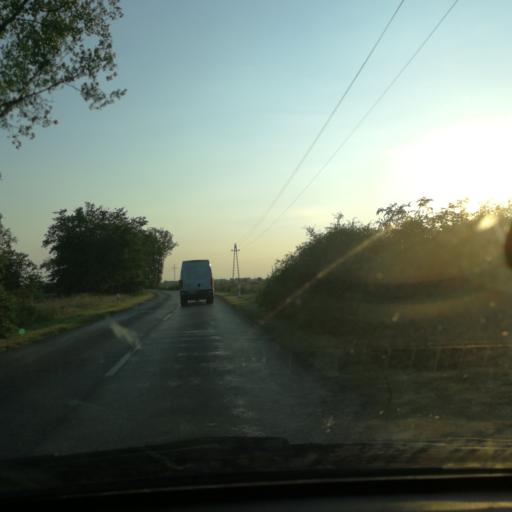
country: HU
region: Bacs-Kiskun
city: Kiskunhalas
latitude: 46.4362
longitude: 19.5461
